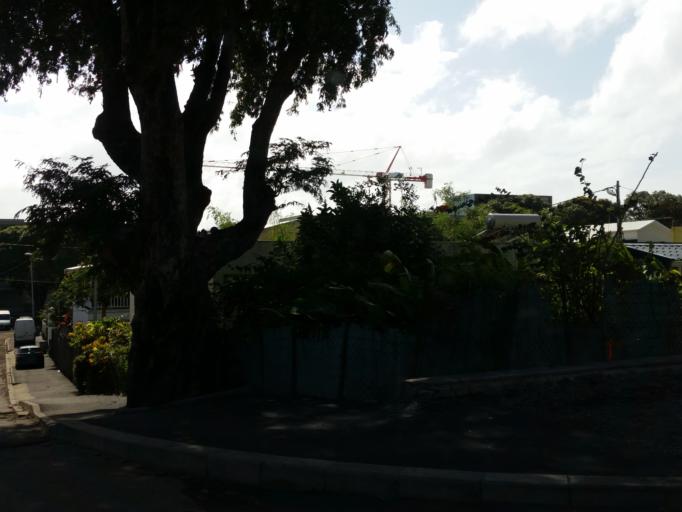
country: RE
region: Reunion
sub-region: Reunion
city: Saint-Denis
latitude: -20.8925
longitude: 55.4627
